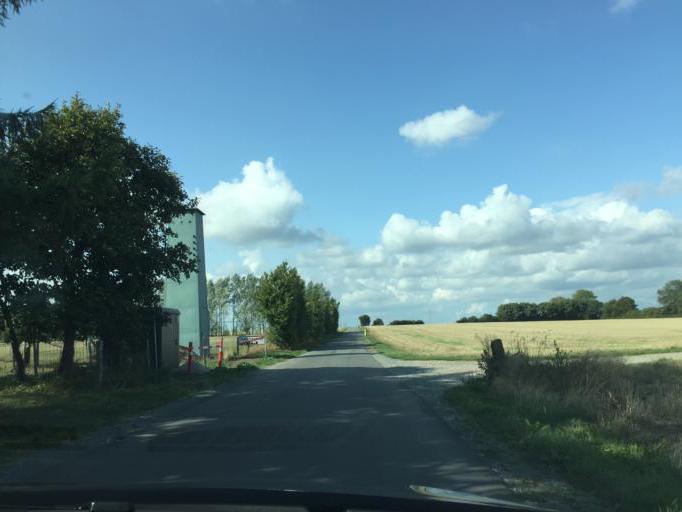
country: DK
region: South Denmark
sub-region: Odense Kommune
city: Bellinge
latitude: 55.3113
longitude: 10.3775
